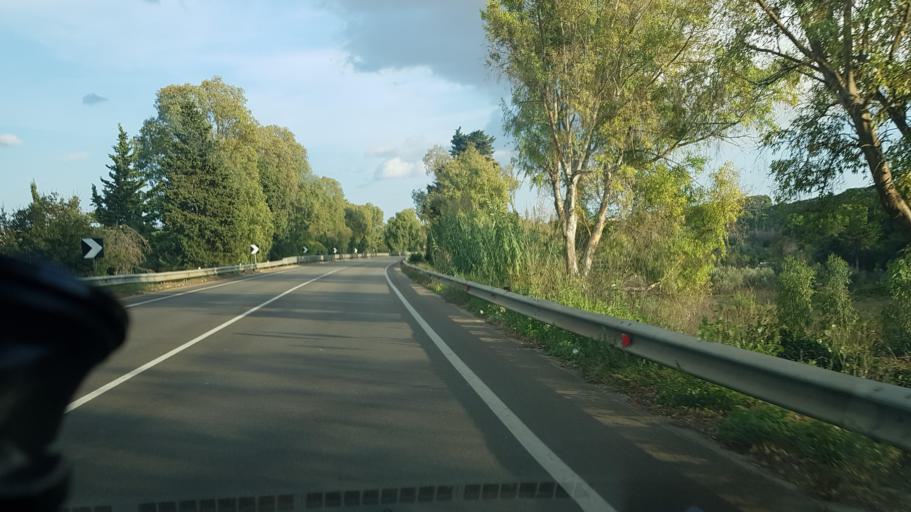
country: IT
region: Apulia
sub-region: Provincia di Lecce
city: Acquarica del Capo
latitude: 39.9053
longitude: 18.2427
